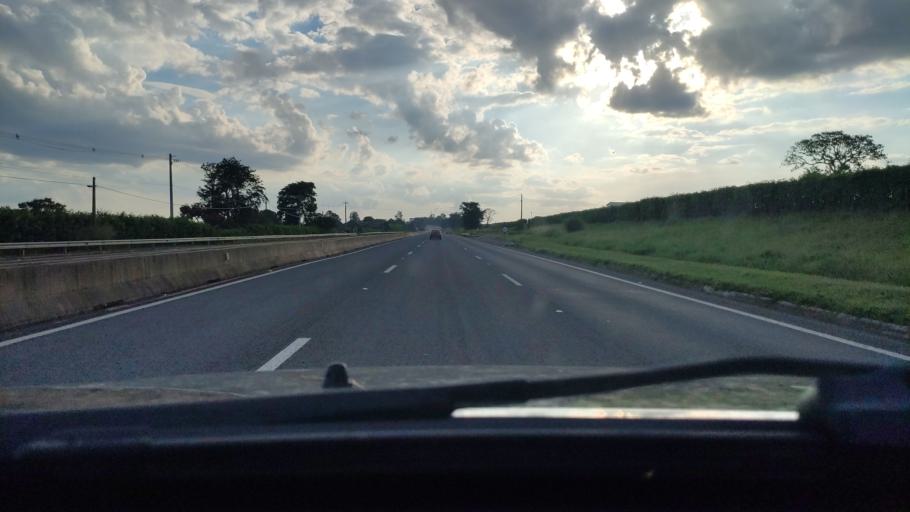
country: BR
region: Sao Paulo
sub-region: Mogi-Mirim
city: Mogi Mirim
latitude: -22.4503
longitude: -47.0677
